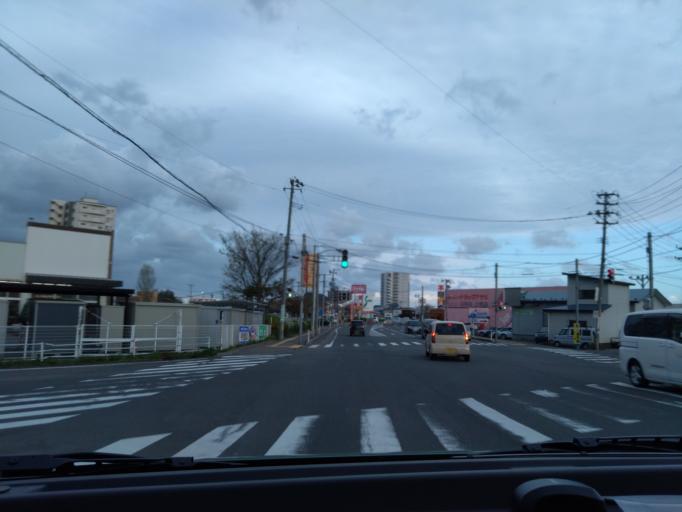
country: JP
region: Akita
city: Akita
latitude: 39.7308
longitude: 140.1452
